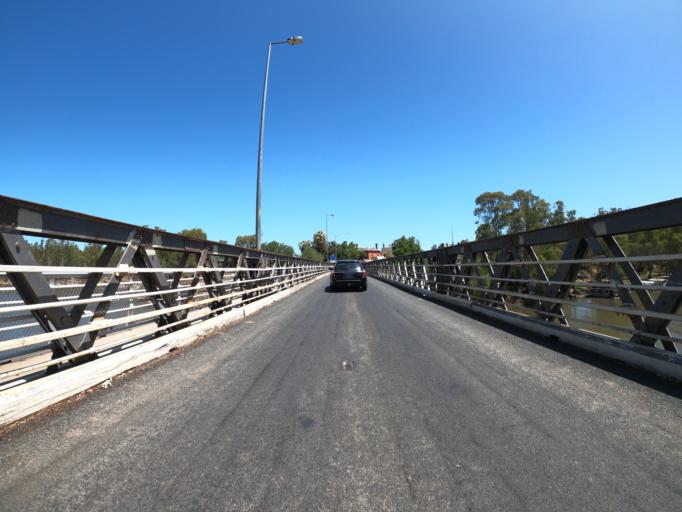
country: AU
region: New South Wales
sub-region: Corowa Shire
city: Corowa
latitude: -36.0065
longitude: 146.3953
